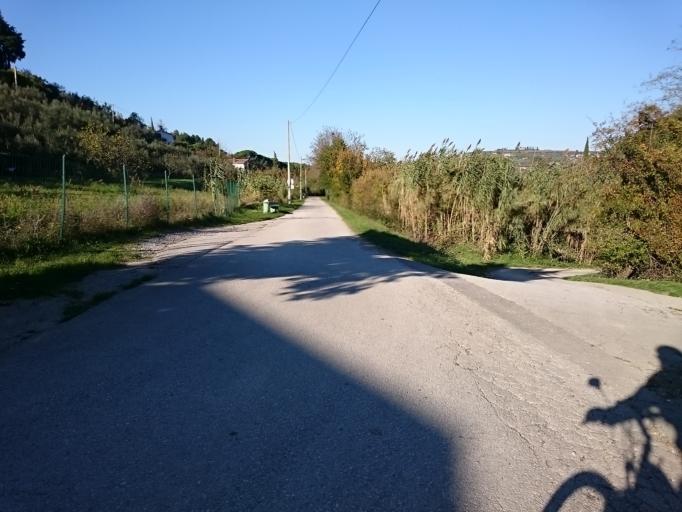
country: SI
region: Piran-Pirano
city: Lucija
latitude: 45.5202
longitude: 13.6070
